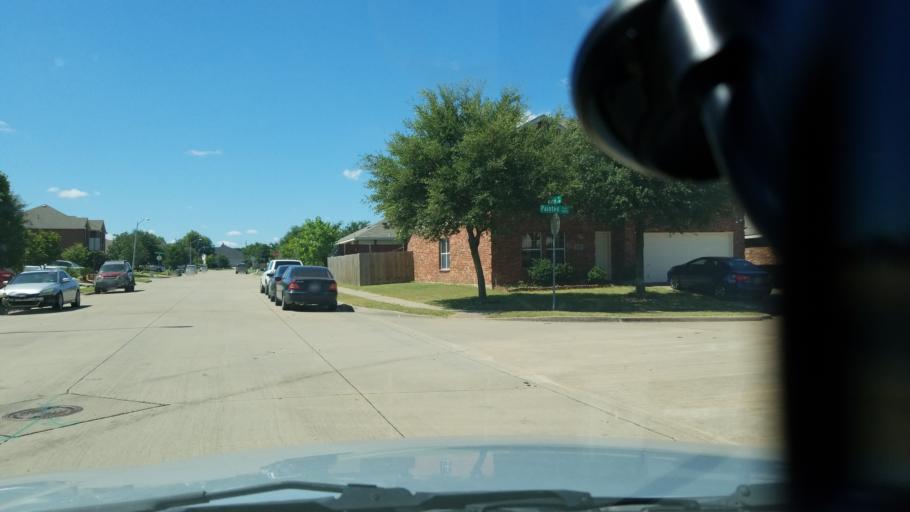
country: US
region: Texas
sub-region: Dallas County
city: Duncanville
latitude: 32.6577
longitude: -96.8649
